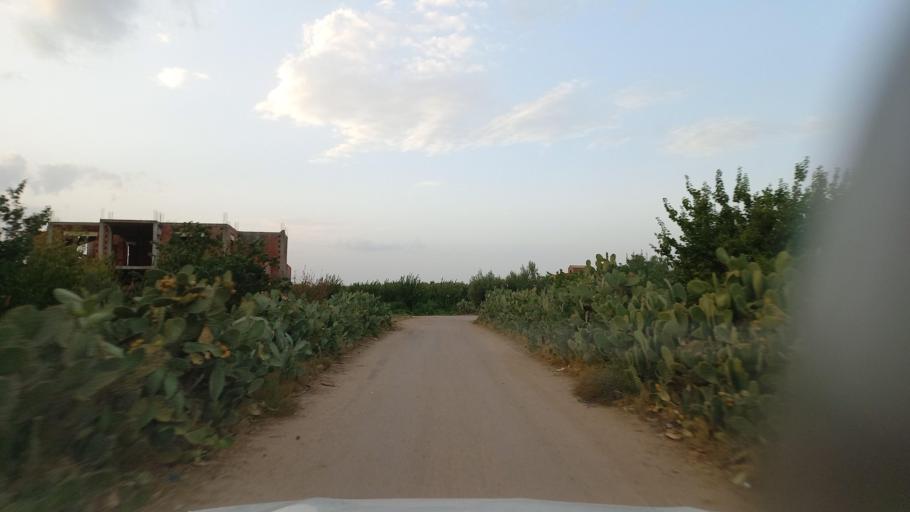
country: TN
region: Al Qasrayn
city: Kasserine
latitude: 35.2731
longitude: 9.0536
